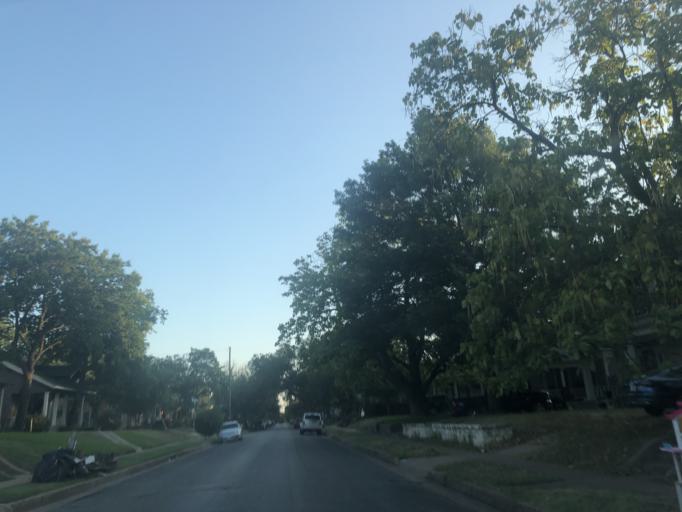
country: US
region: Texas
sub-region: Dallas County
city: Dallas
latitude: 32.7500
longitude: -96.8303
